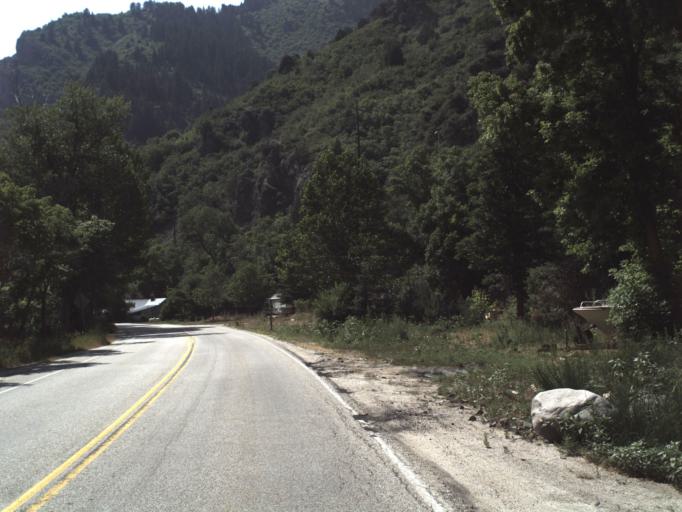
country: US
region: Utah
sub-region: Weber County
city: Liberty
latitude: 41.2548
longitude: -111.8703
